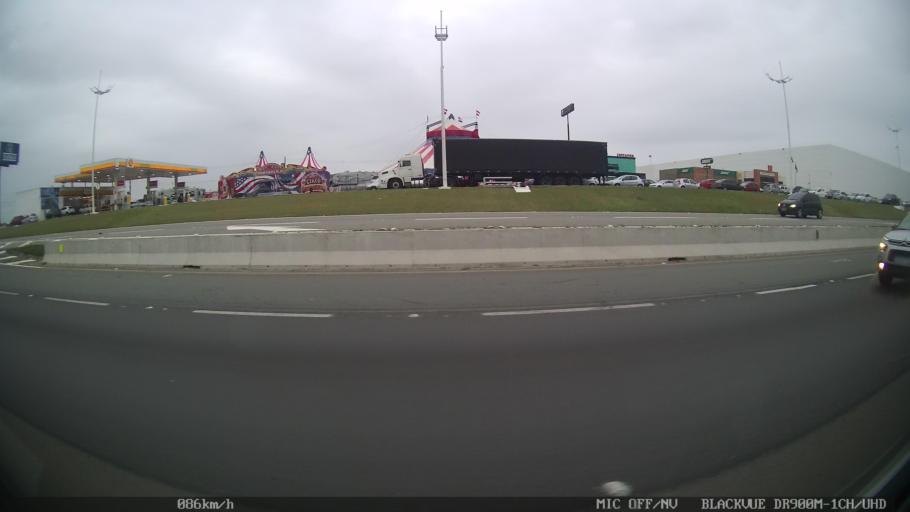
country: BR
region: Santa Catarina
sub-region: Barra Velha
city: Barra Velha
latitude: -26.6371
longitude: -48.6970
